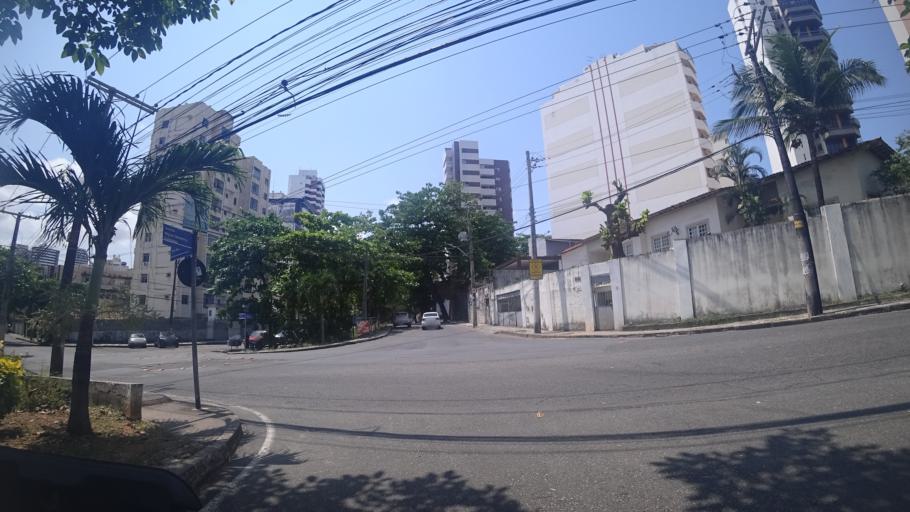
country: BR
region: Bahia
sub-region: Salvador
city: Salvador
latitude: -12.9946
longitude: -38.4528
